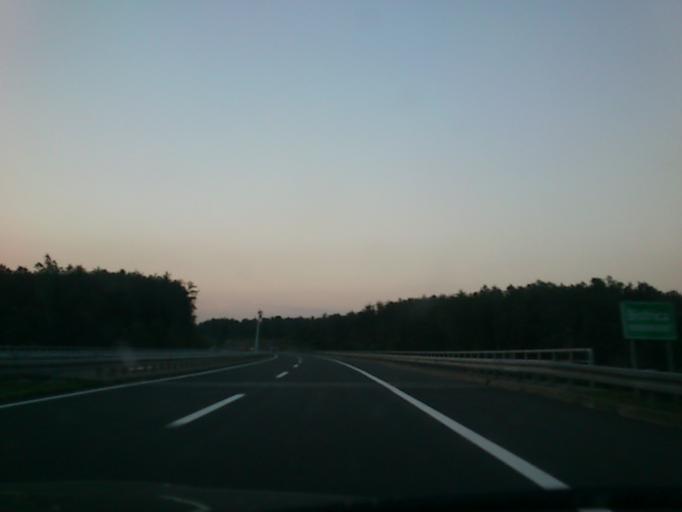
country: HR
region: Karlovacka
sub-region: Grad Ogulin
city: Ogulin
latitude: 45.2965
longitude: 15.2774
